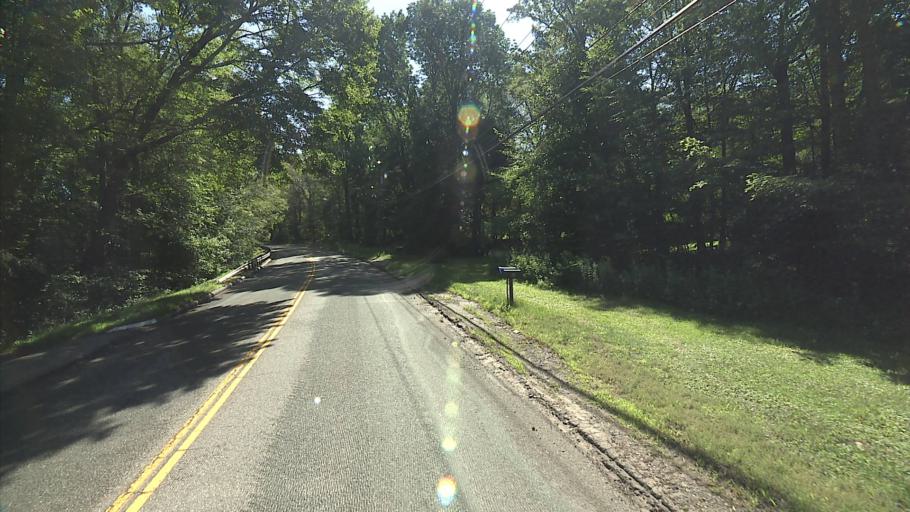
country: US
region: Connecticut
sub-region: Middlesex County
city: East Hampton
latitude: 41.5639
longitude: -72.5038
